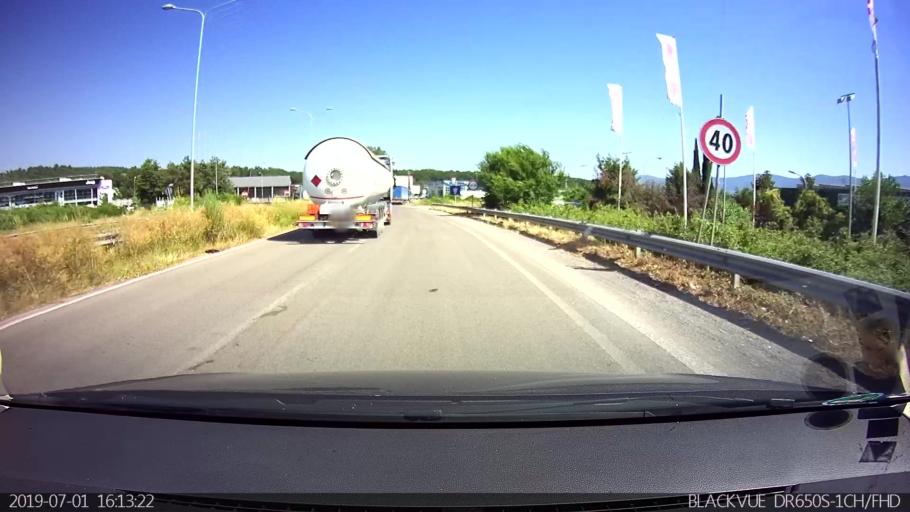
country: IT
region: Latium
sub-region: Provincia di Frosinone
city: Ceccano
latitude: 41.6080
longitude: 13.2993
